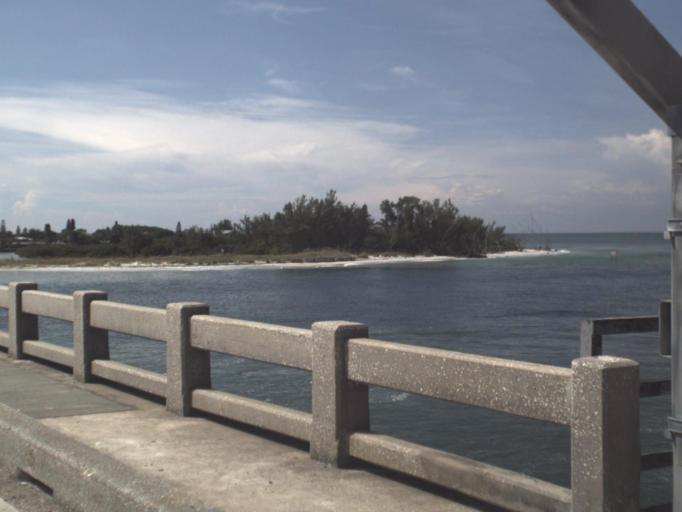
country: US
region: Florida
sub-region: Manatee County
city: Cortez
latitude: 27.4446
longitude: -82.6881
